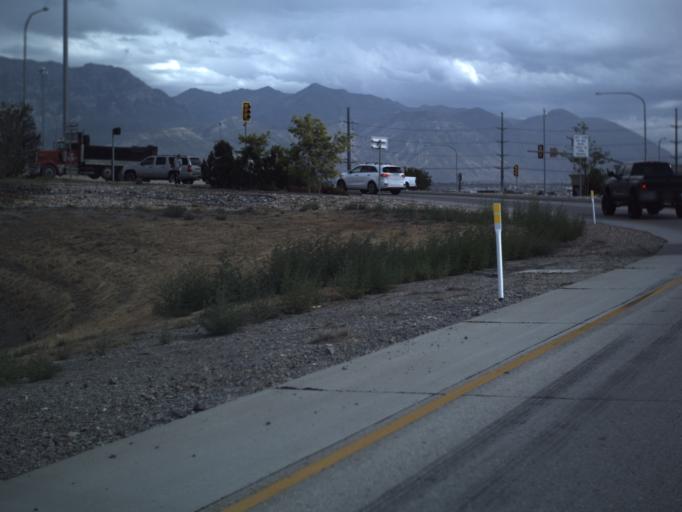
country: US
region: Utah
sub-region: Utah County
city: American Fork
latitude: 40.3604
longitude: -111.7868
